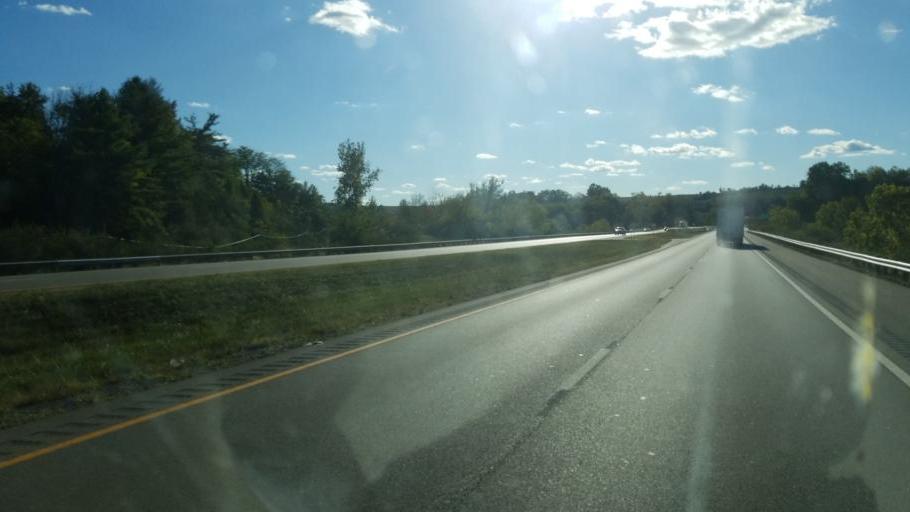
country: US
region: Ohio
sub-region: Belmont County
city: Barnesville
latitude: 40.0591
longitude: -81.1445
